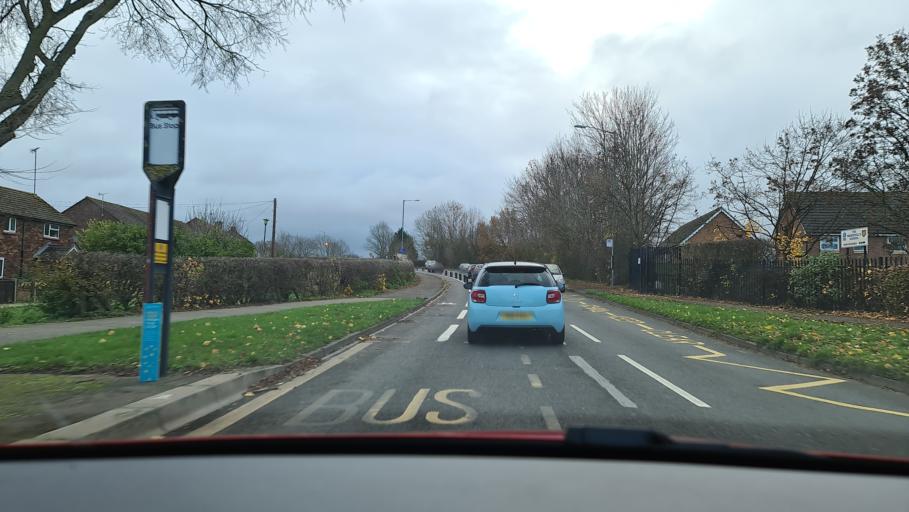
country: GB
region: England
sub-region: Buckinghamshire
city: Aylesbury
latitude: 51.8000
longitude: -0.8128
